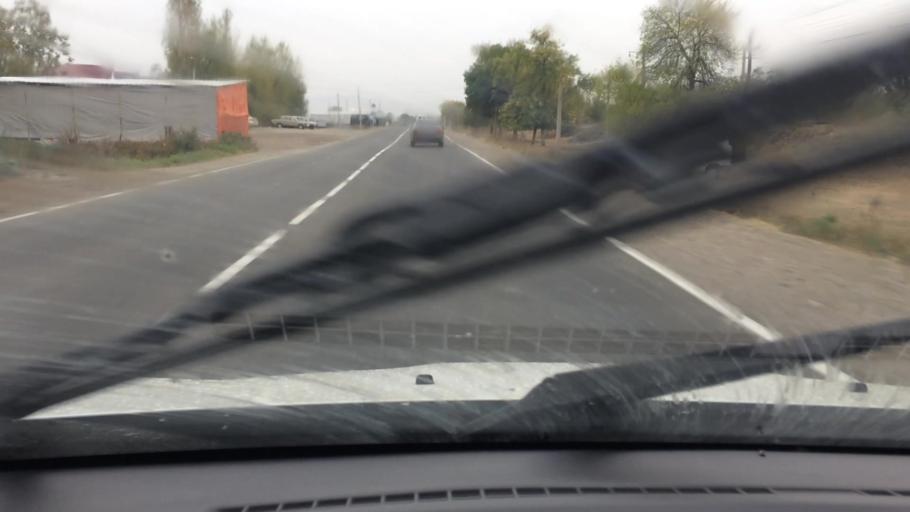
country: GE
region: Kvemo Kartli
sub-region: Marneuli
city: Marneuli
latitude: 41.4207
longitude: 44.8250
